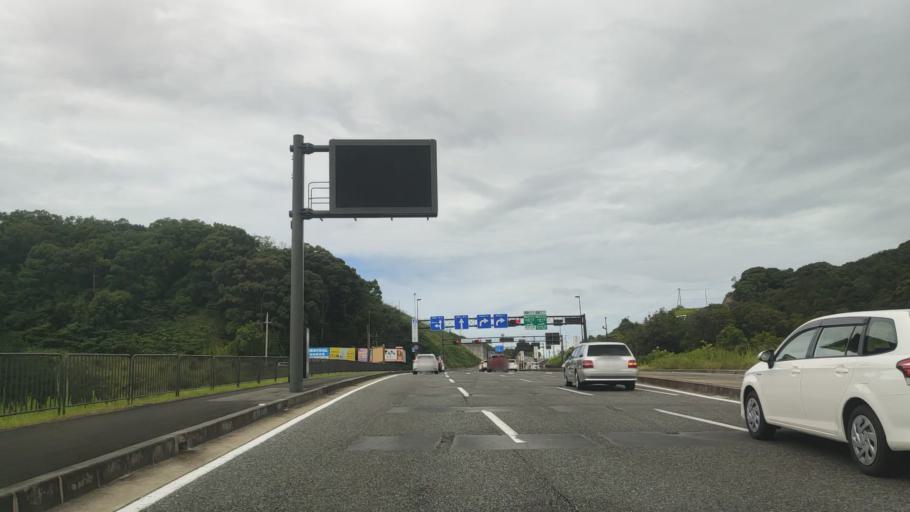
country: JP
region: Wakayama
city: Tanabe
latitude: 33.7455
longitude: 135.3697
